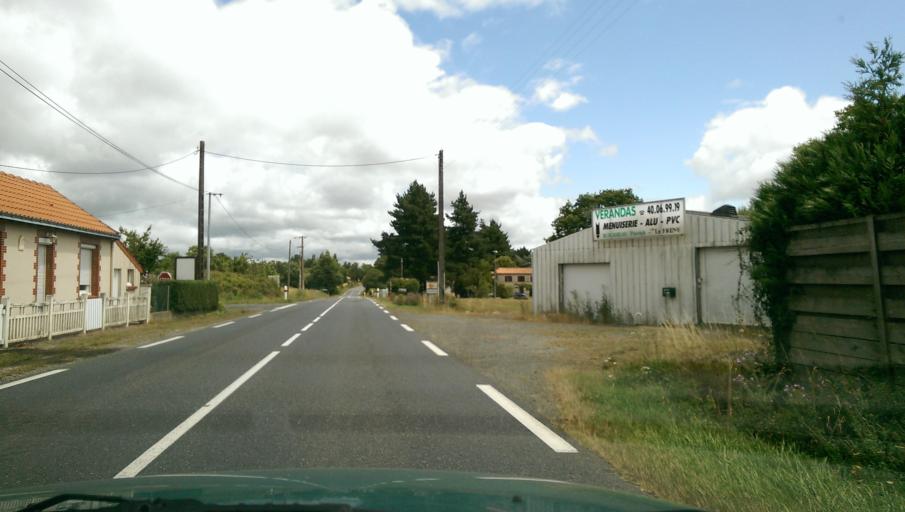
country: FR
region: Pays de la Loire
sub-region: Departement de la Loire-Atlantique
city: Remouille
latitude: 47.0736
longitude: -1.3751
